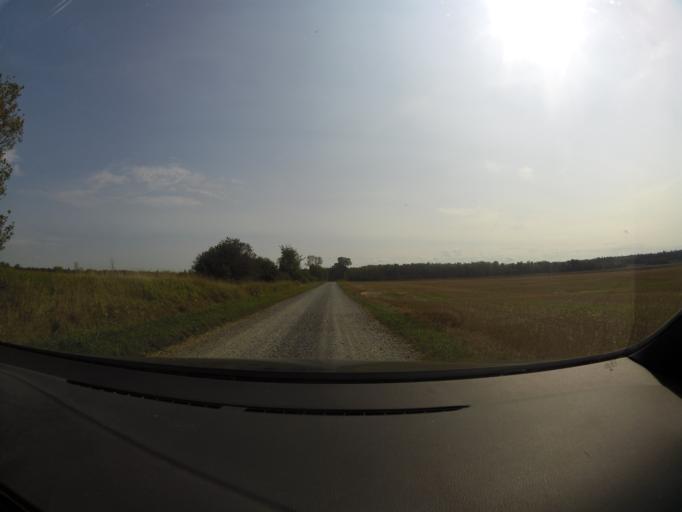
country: CA
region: Ontario
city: Carleton Place
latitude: 45.2843
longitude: -76.2126
